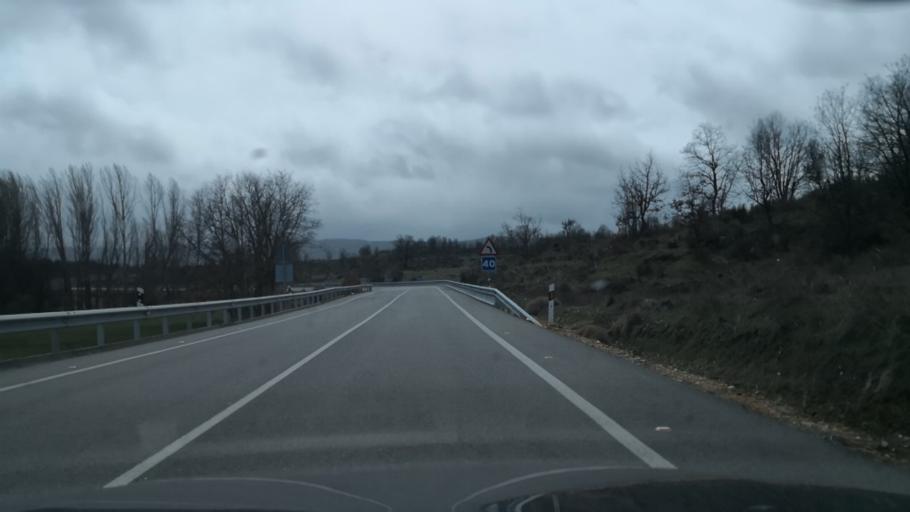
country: ES
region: Castille and Leon
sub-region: Provincia de Zamora
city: Ferreras de Arriba
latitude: 41.9633
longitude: -6.2184
